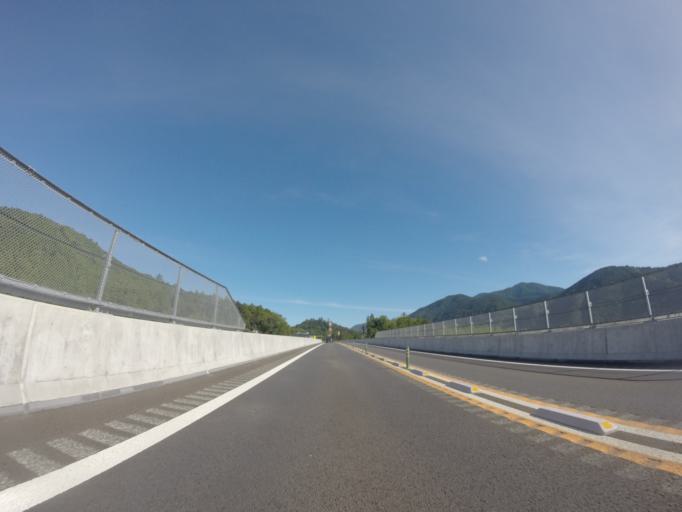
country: JP
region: Shizuoka
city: Fujinomiya
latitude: 35.2481
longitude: 138.4741
